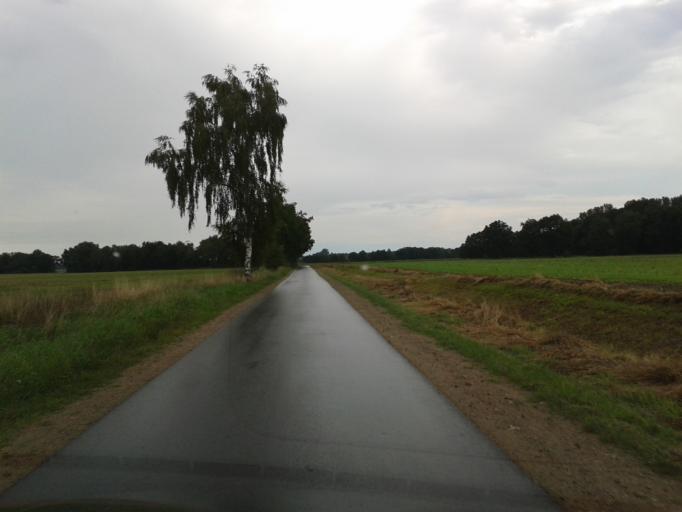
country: DE
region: Lower Saxony
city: Woltersdorf
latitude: 52.9456
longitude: 11.1958
